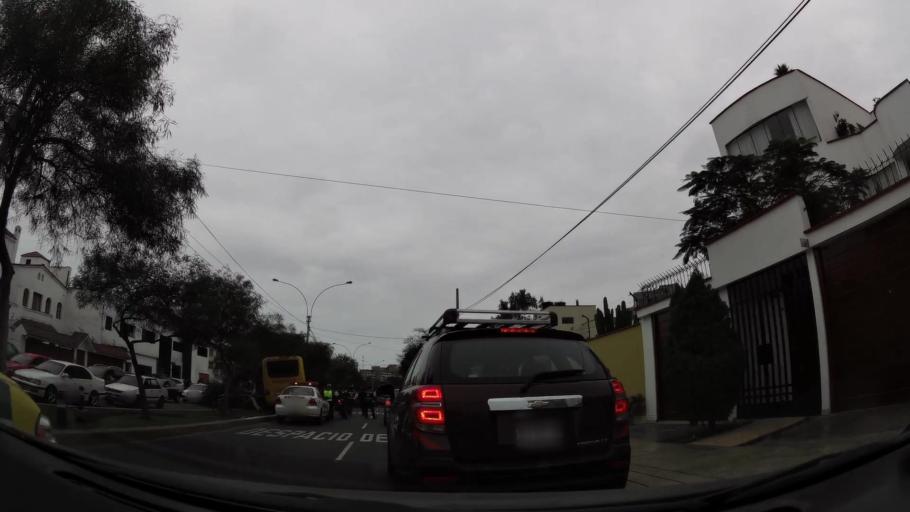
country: PE
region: Lima
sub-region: Lima
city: San Isidro
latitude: -12.0883
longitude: -77.0486
